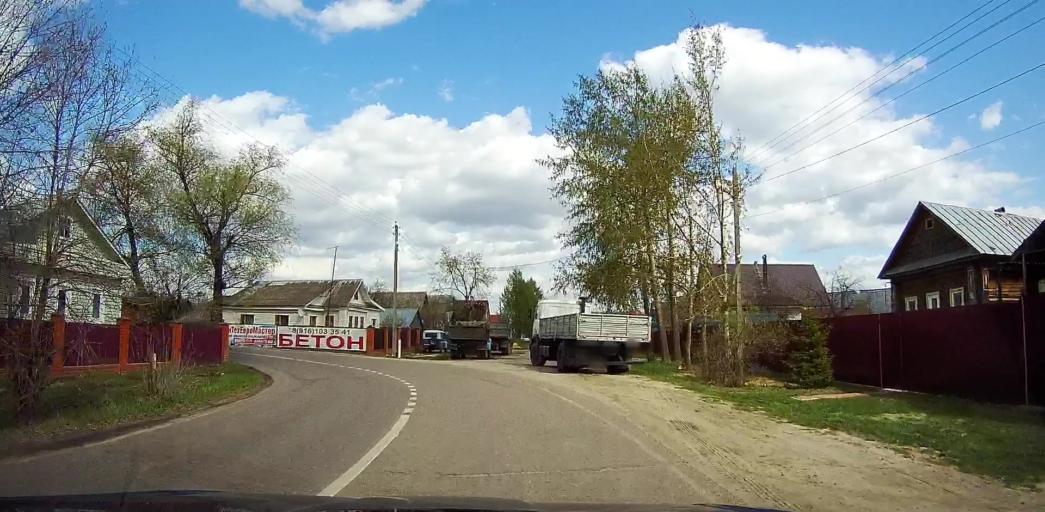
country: RU
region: Moskovskaya
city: Davydovo
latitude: 55.6054
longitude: 38.8479
